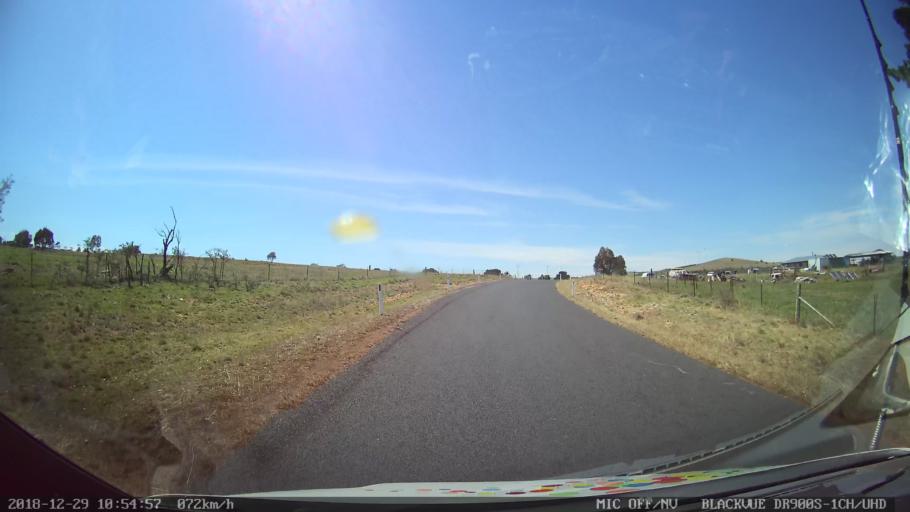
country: AU
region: New South Wales
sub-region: Palerang
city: Bungendore
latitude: -35.1194
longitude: 149.5306
